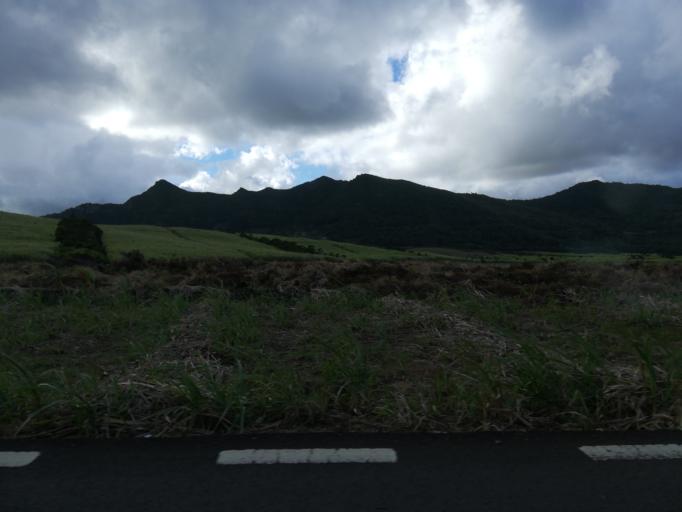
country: MU
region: Flacq
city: Clemencia
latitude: -20.2603
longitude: 57.6999
